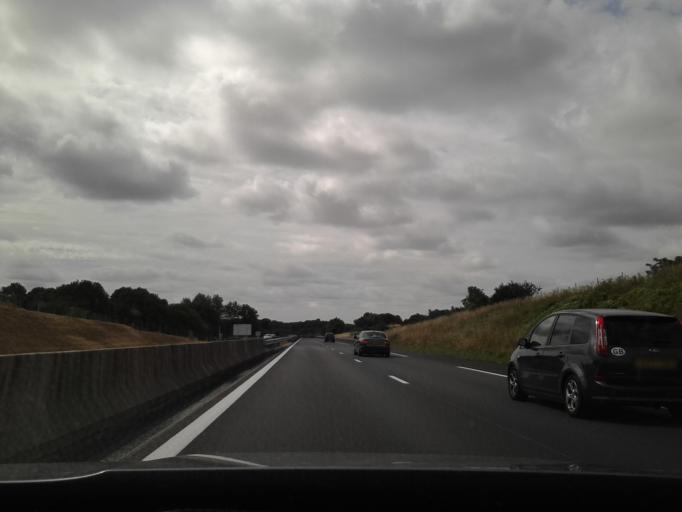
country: FR
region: Lower Normandy
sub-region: Departement de l'Orne
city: Sees
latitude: 48.5624
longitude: 0.1758
